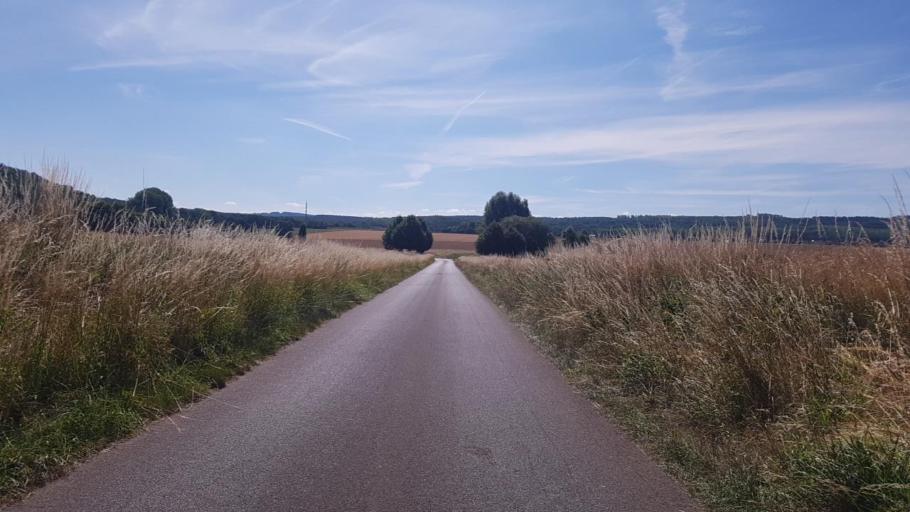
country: DE
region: North Rhine-Westphalia
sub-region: Regierungsbezirk Koln
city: Mechernich
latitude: 50.5980
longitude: 6.6147
